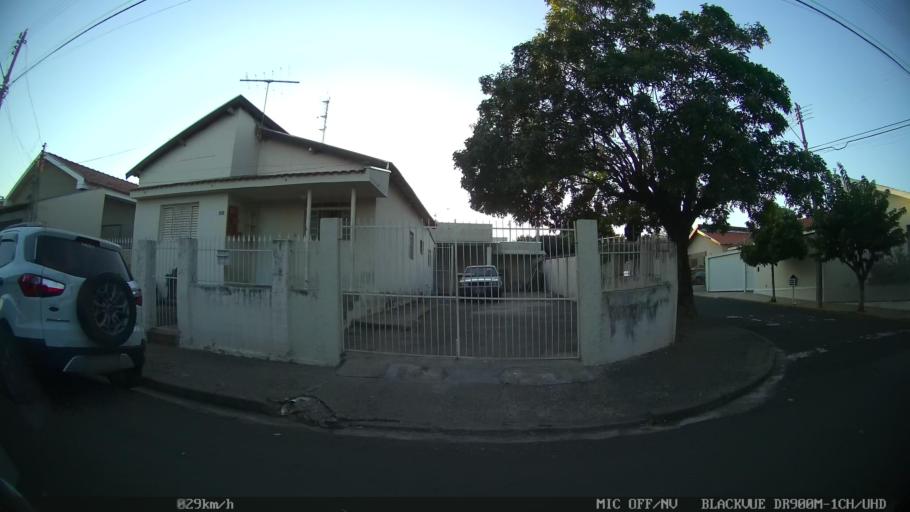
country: BR
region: Sao Paulo
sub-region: Sao Jose Do Rio Preto
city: Sao Jose do Rio Preto
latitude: -20.8021
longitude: -49.3670
